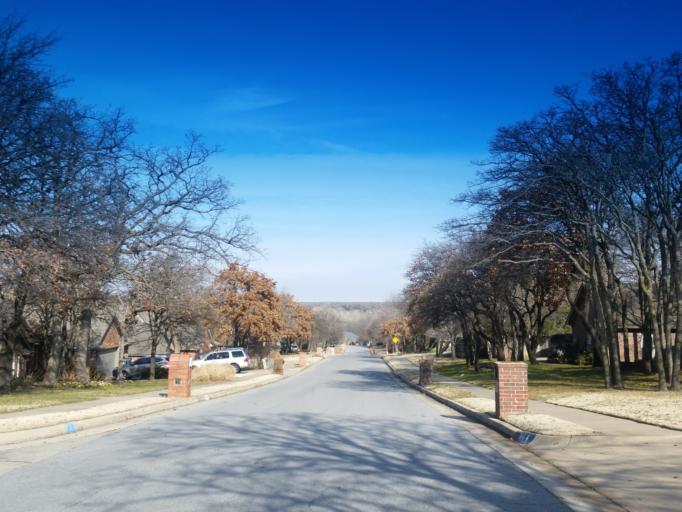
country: US
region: Oklahoma
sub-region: Oklahoma County
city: Edmond
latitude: 35.6444
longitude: -97.4332
